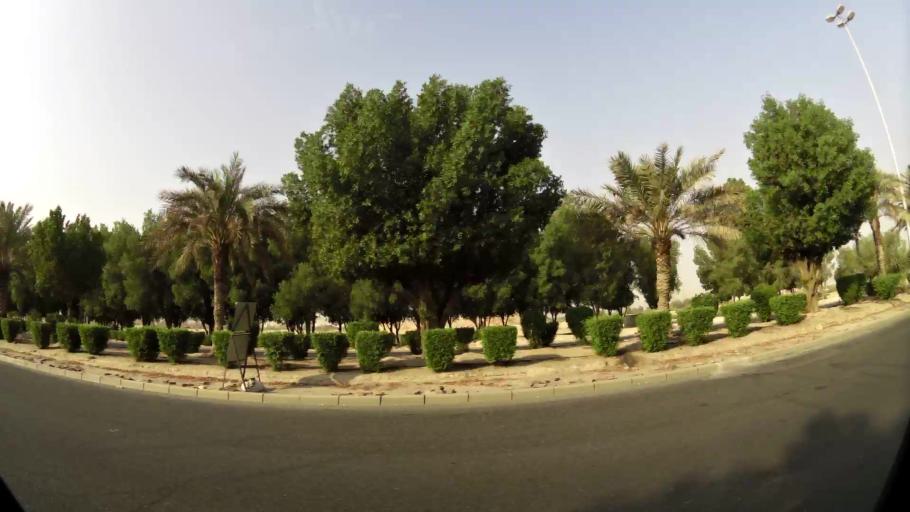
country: KW
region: Al Asimah
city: Ar Rabiyah
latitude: 29.3166
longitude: 47.8056
